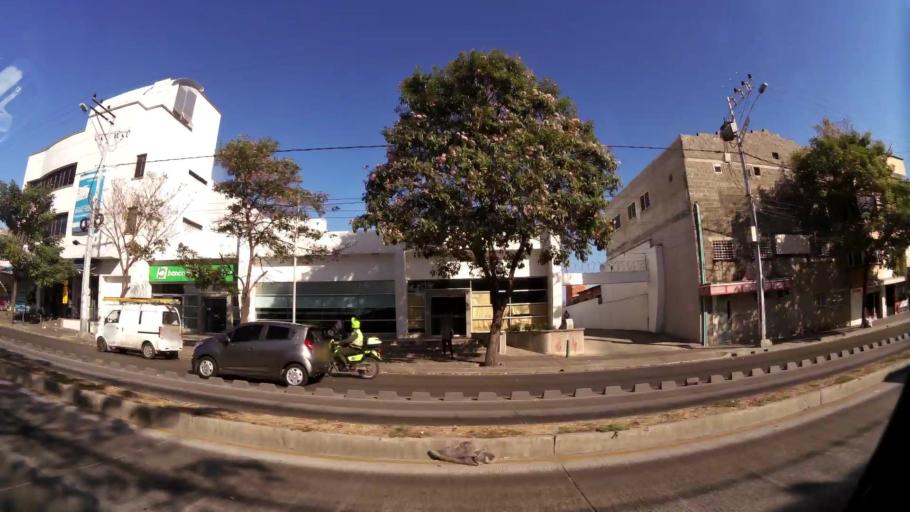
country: CO
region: Atlantico
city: Barranquilla
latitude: 10.9712
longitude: -74.7897
